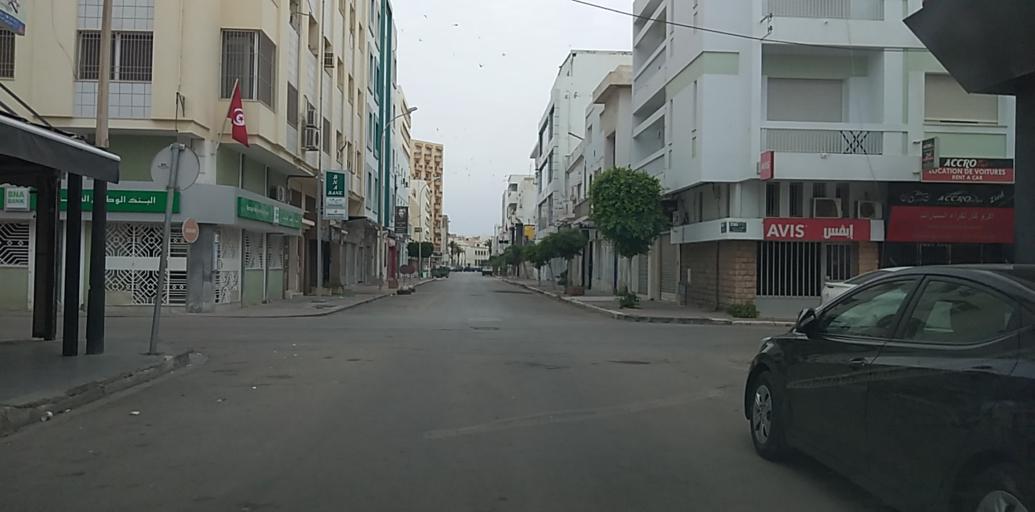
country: TN
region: Safaqis
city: Sfax
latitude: 34.7300
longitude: 10.7653
